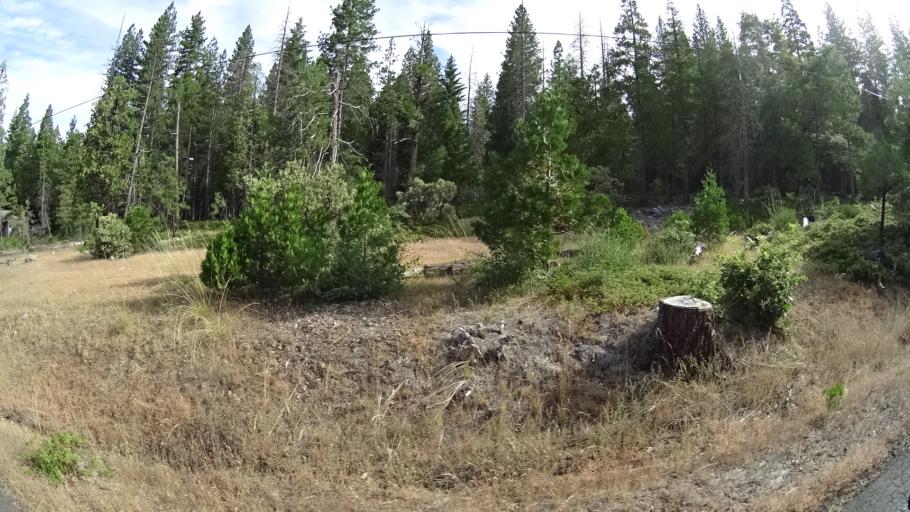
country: US
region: California
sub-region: Calaveras County
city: Arnold
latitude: 38.2669
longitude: -120.3256
